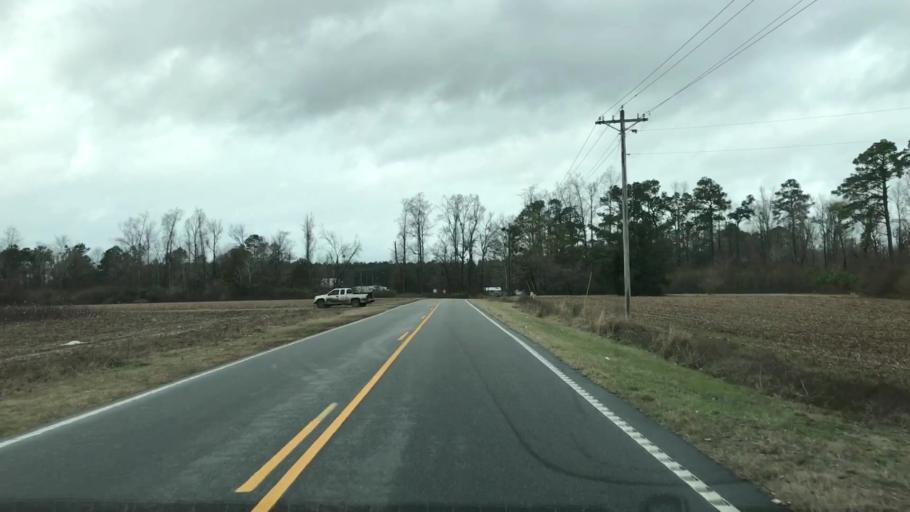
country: US
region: South Carolina
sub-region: Florence County
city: Johnsonville
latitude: 33.6532
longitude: -79.3024
